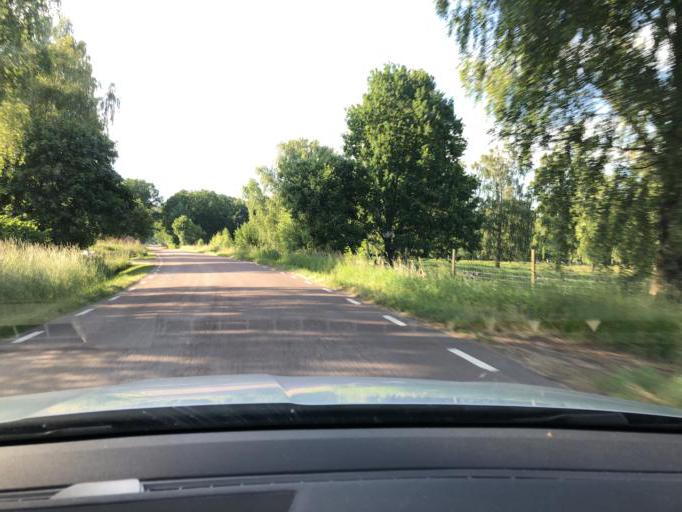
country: SE
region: Blekinge
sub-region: Solvesborgs Kommun
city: Soelvesborg
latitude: 56.1576
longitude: 14.6012
